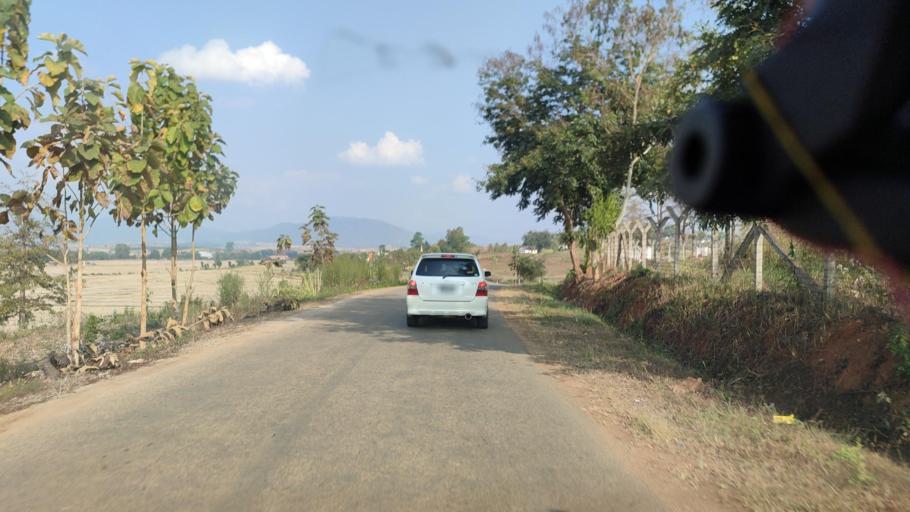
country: CN
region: Yunnan
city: Nayun
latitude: 21.8449
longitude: 99.6709
